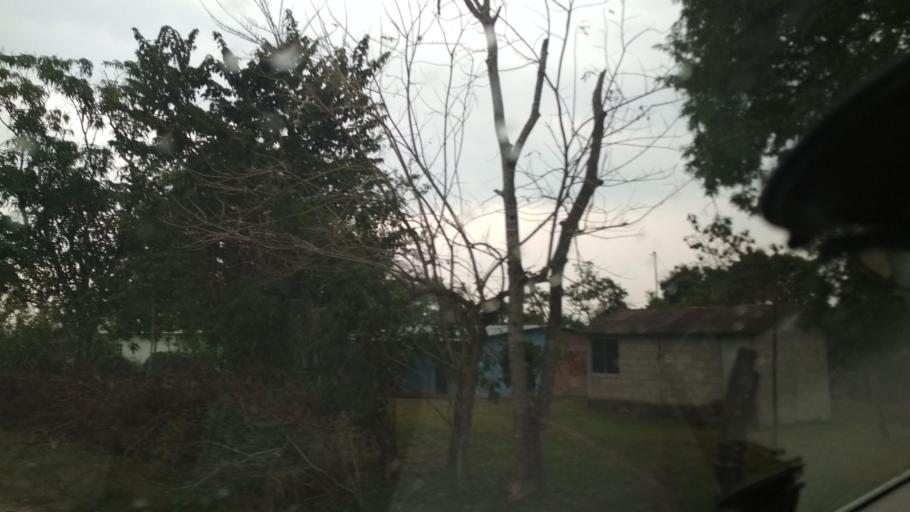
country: MM
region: Shan
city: Taunggyi
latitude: 20.3339
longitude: 97.3100
